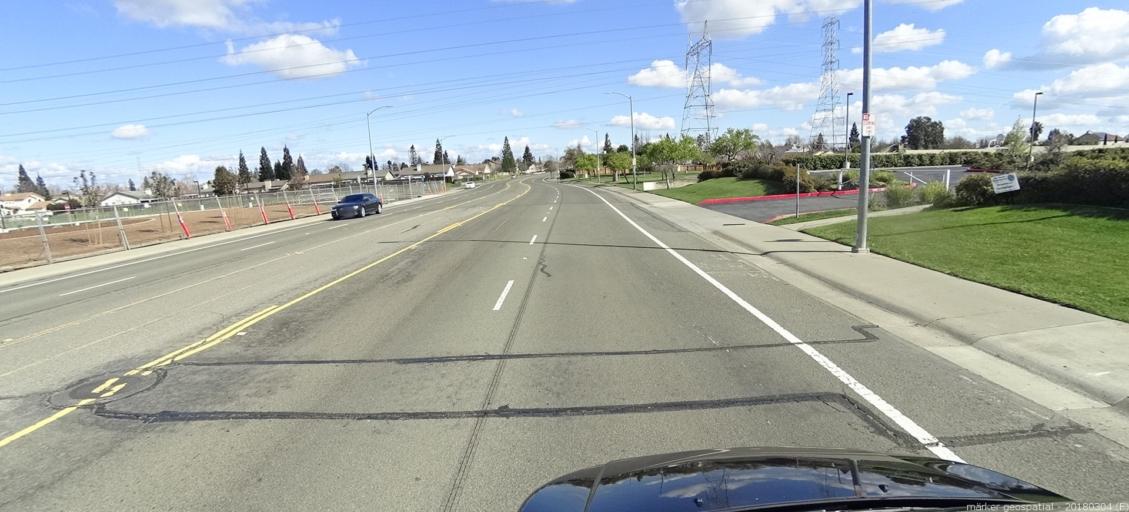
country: US
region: California
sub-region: Sacramento County
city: Vineyard
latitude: 38.4639
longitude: -121.3529
